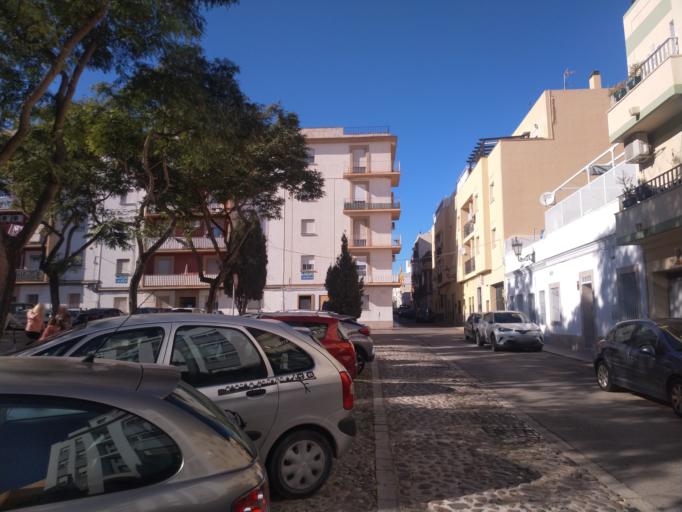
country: ES
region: Andalusia
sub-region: Provincia de Cadiz
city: San Fernando
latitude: 36.4704
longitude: -6.1919
